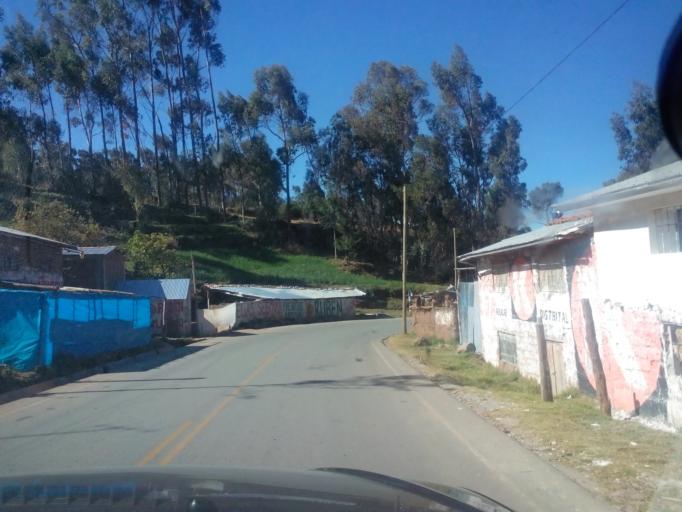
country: PE
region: Apurimac
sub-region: Provincia de Andahuaylas
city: Talavera
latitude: -13.6523
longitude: -73.5144
